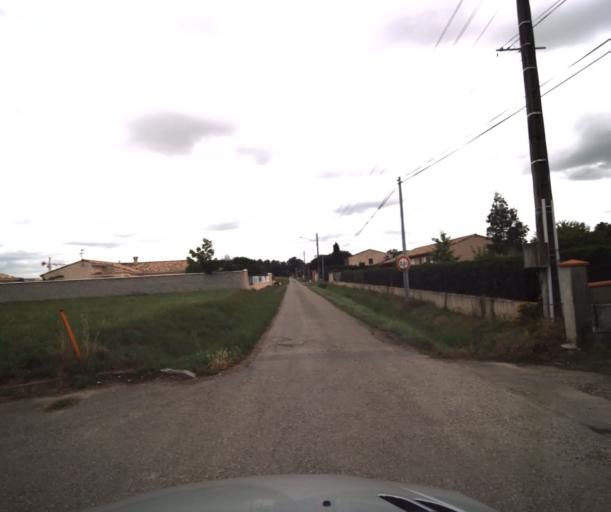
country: FR
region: Midi-Pyrenees
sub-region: Departement de la Haute-Garonne
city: Labarthe-sur-Leze
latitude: 43.4634
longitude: 1.3921
